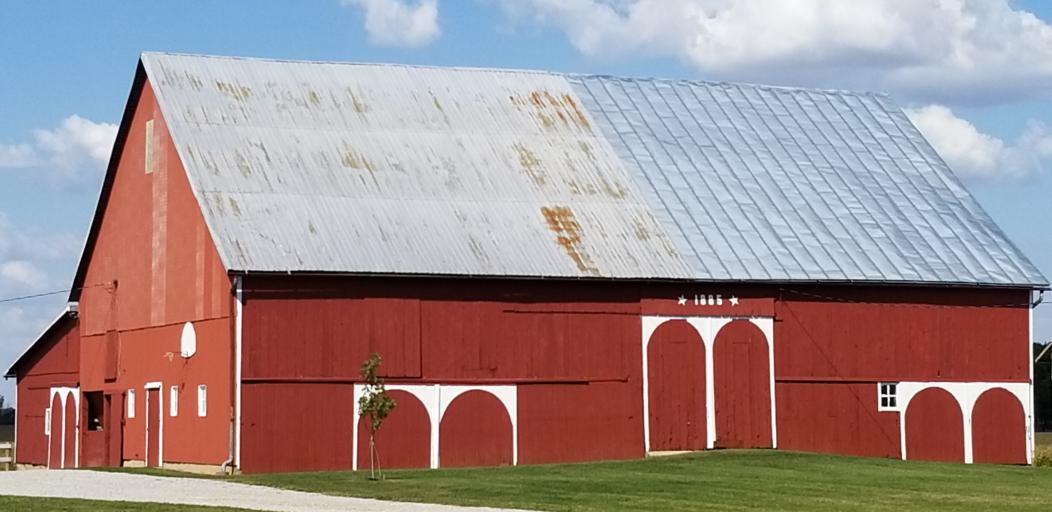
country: US
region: Ohio
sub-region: Shelby County
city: Botkins
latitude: 40.4670
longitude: -84.2717
